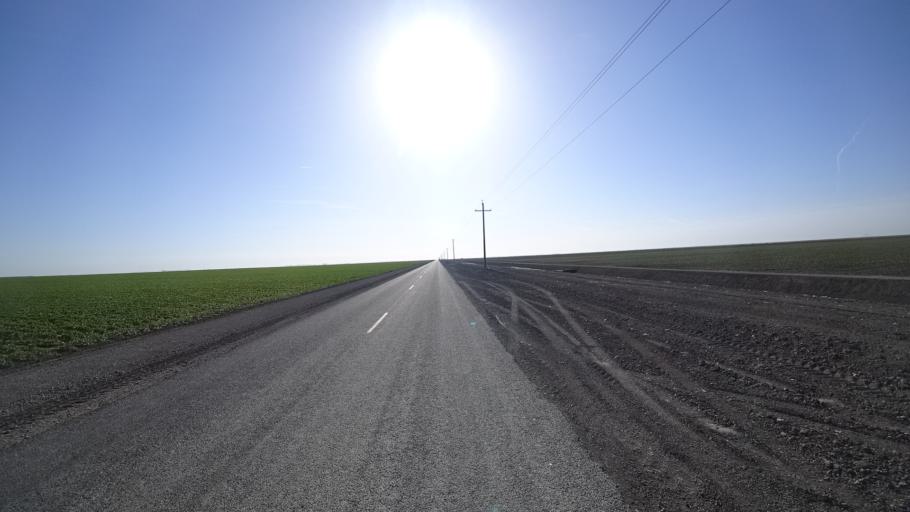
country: US
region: California
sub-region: Kings County
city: Stratford
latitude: 36.0797
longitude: -119.7409
